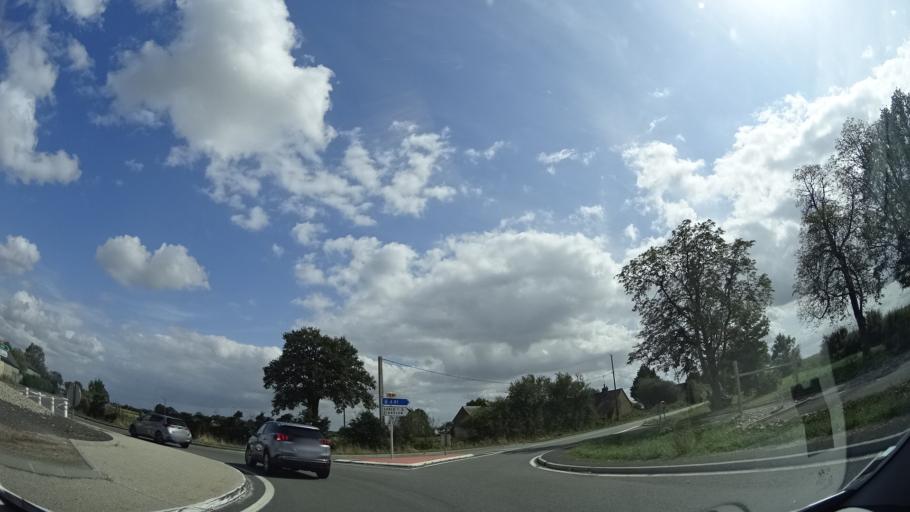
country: FR
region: Pays de la Loire
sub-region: Departement de la Sarthe
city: Brulon
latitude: 48.0213
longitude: -0.2149
